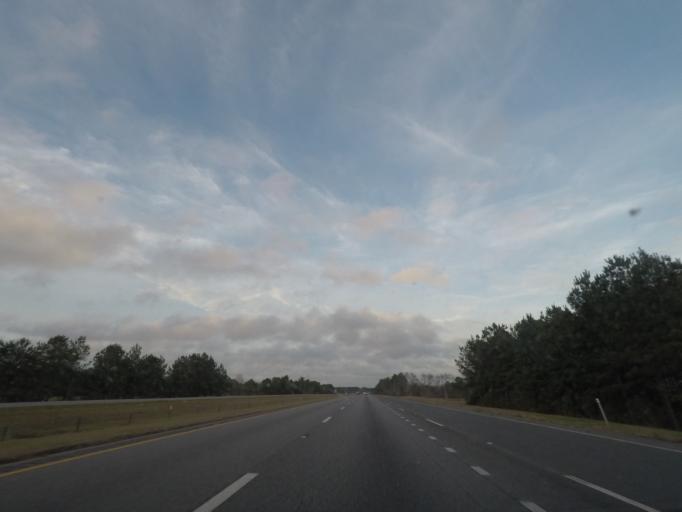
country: US
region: South Carolina
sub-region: Orangeburg County
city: Holly Hill
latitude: 33.3878
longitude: -80.5166
